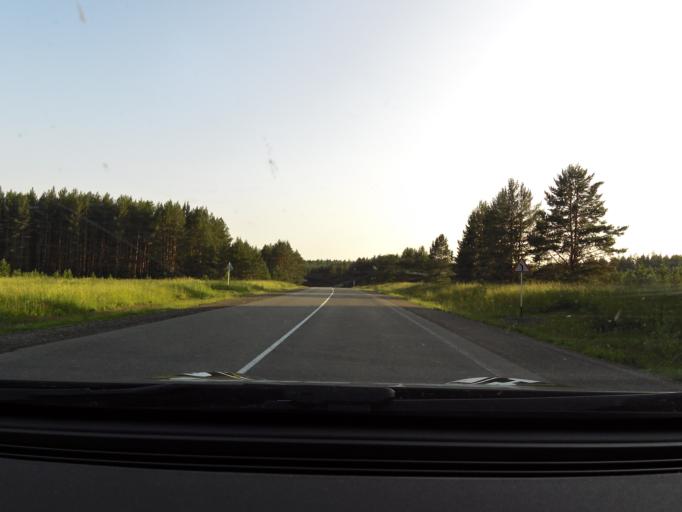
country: RU
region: Sverdlovsk
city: Nizhniye Sergi
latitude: 56.6341
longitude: 59.2443
